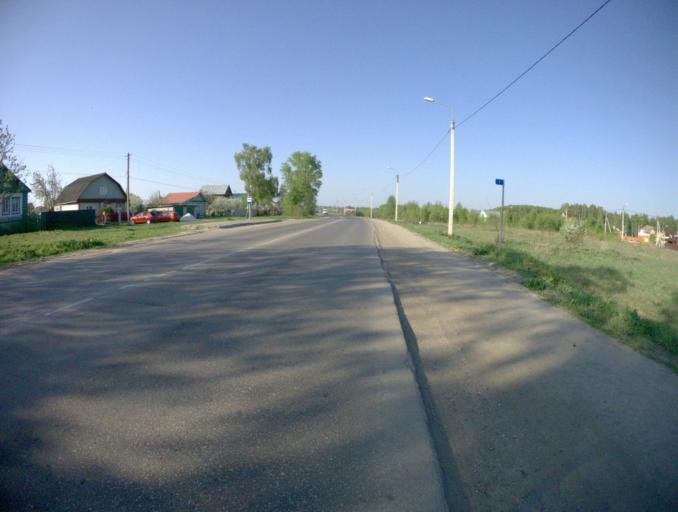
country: RU
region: Vladimir
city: Novovyazniki
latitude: 56.2242
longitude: 42.1879
